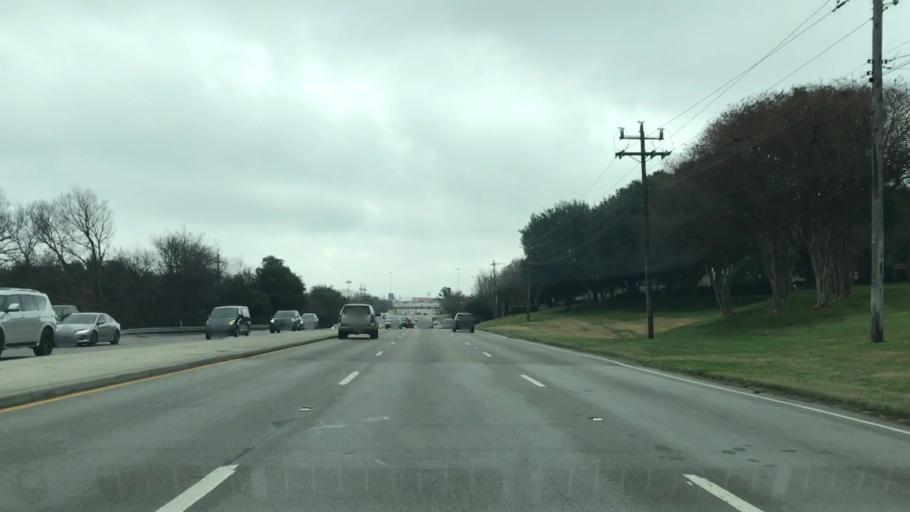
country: US
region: Texas
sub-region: Dallas County
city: University Park
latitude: 32.8635
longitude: -96.7591
